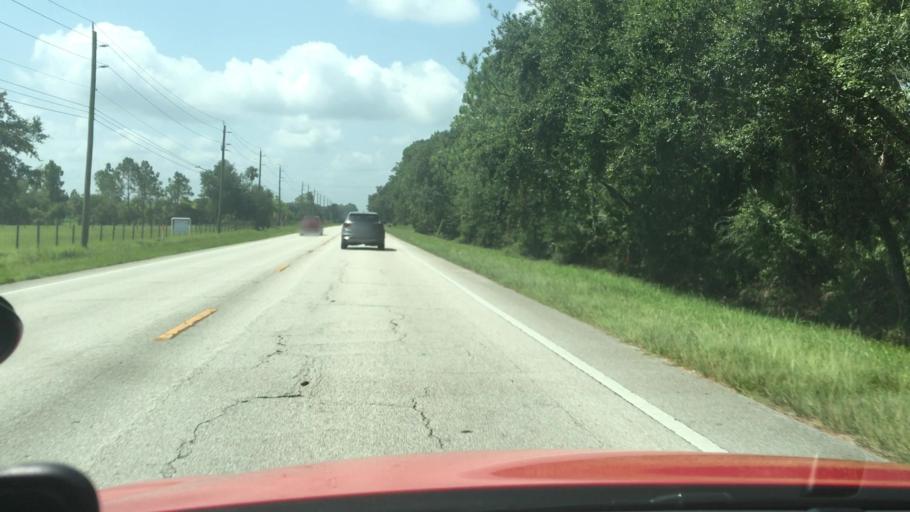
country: US
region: Florida
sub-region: Volusia County
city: Samsula-Spruce Creek
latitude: 29.0546
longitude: -81.0684
